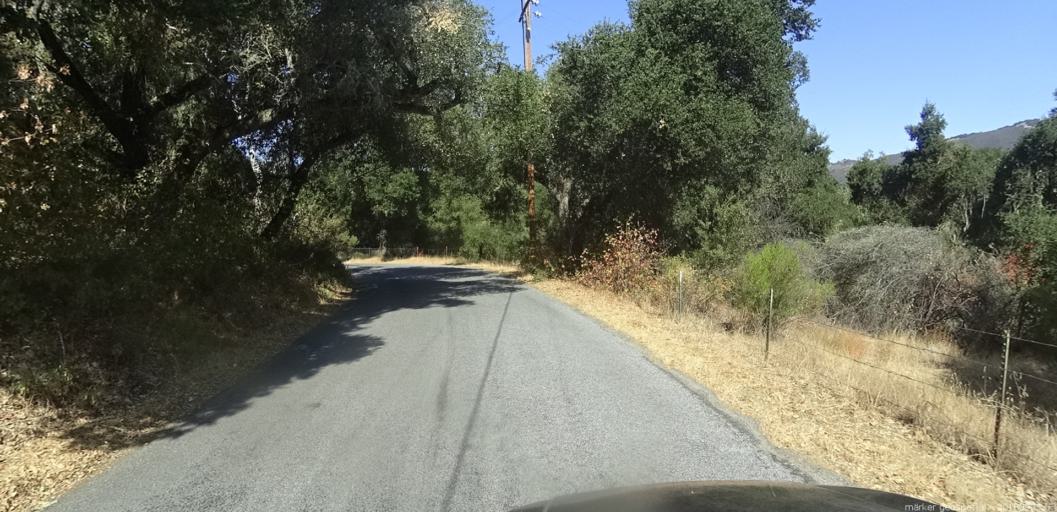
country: US
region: California
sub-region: Monterey County
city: Carmel Valley Village
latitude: 36.3962
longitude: -121.6477
